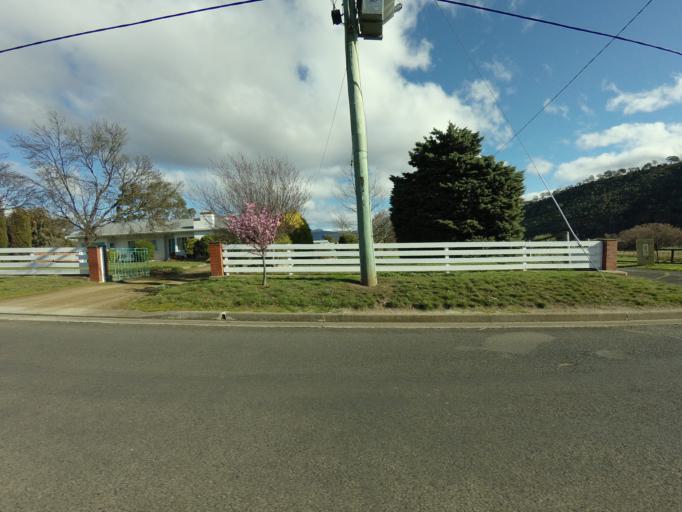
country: AU
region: Tasmania
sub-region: Derwent Valley
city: New Norfolk
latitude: -42.7551
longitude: 147.0503
